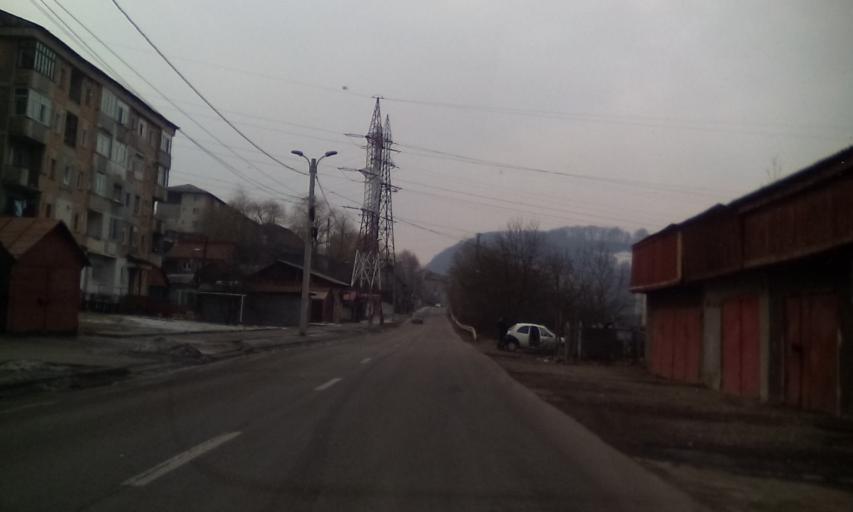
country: RO
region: Hunedoara
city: Lupeni
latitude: 45.3560
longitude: 23.2107
